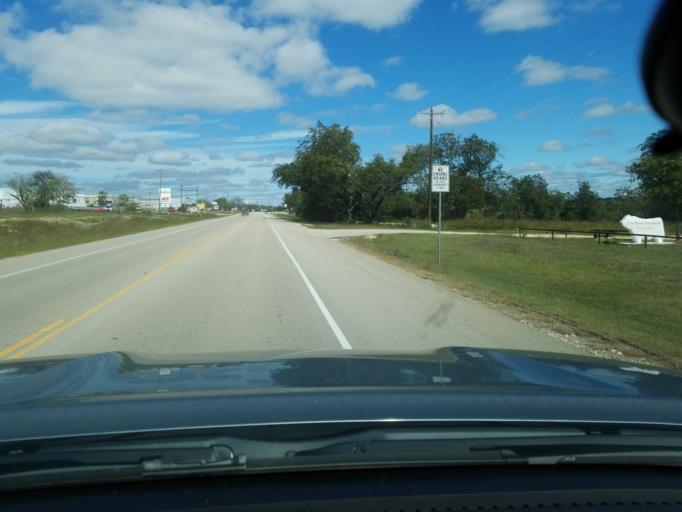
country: US
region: Texas
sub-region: Hamilton County
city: Hamilton
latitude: 31.6883
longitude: -98.1305
